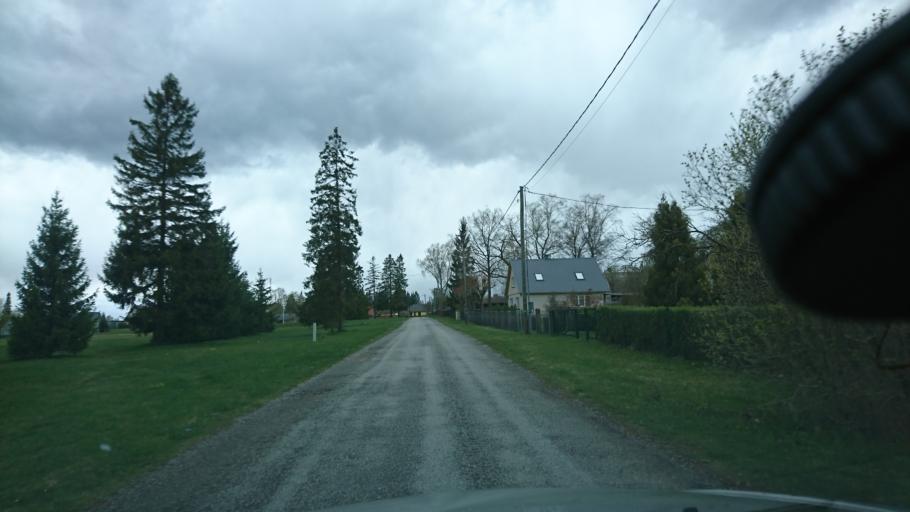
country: EE
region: Laeaene-Virumaa
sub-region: Tapa vald
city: Tapa
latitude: 59.2554
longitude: 25.9684
